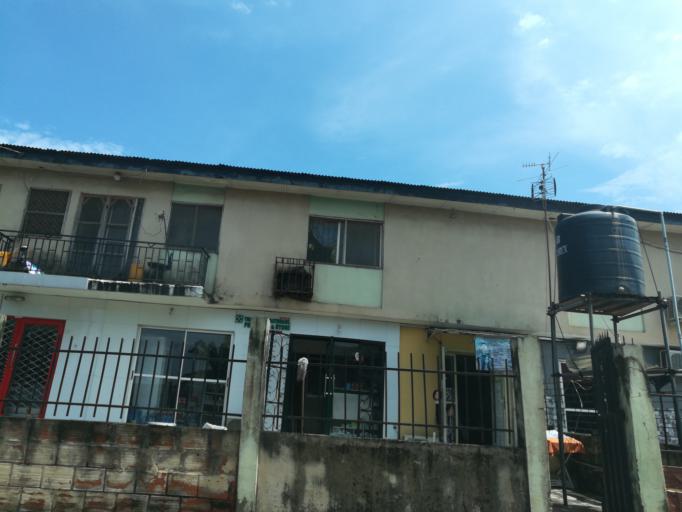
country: NG
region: Lagos
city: Agege
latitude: 6.6064
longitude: 3.3269
